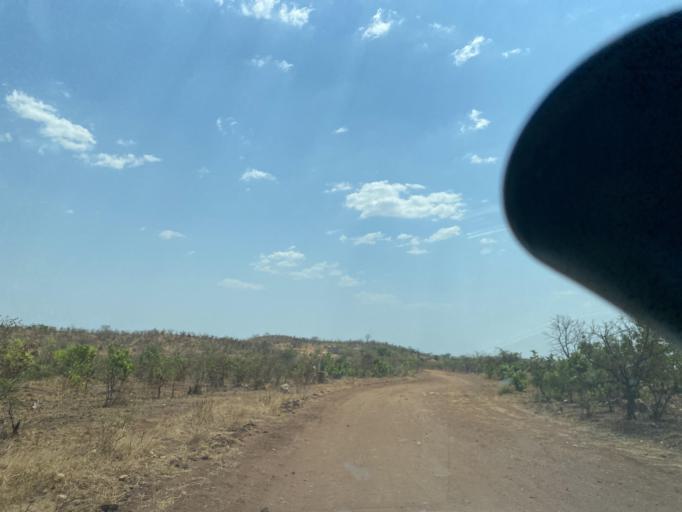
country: ZM
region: Lusaka
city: Lusaka
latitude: -15.4990
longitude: 27.9482
